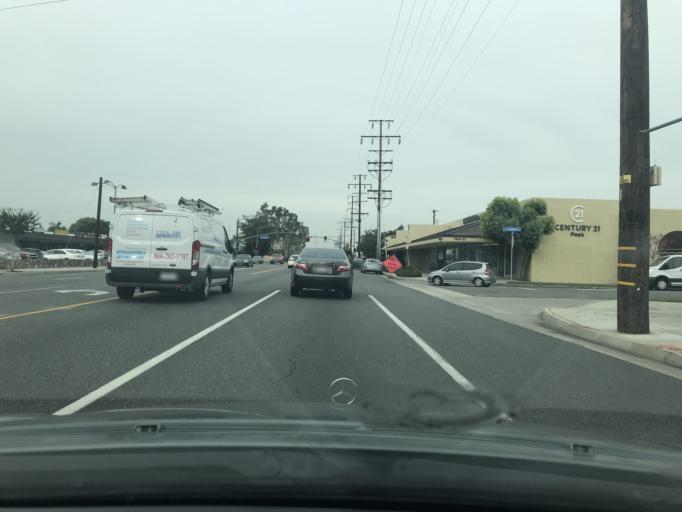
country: US
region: California
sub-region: Los Angeles County
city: Downey
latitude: 33.9552
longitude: -118.1330
